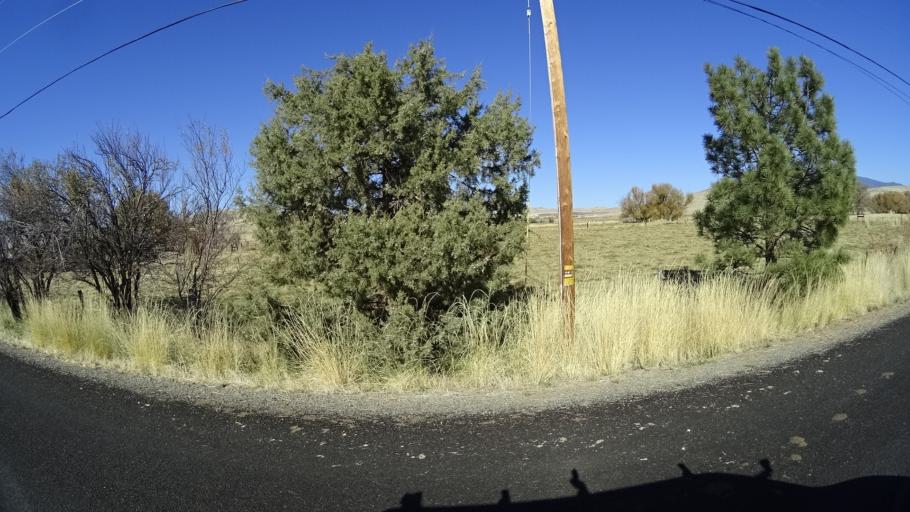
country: US
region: California
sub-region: Siskiyou County
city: Montague
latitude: 41.7263
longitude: -122.4047
